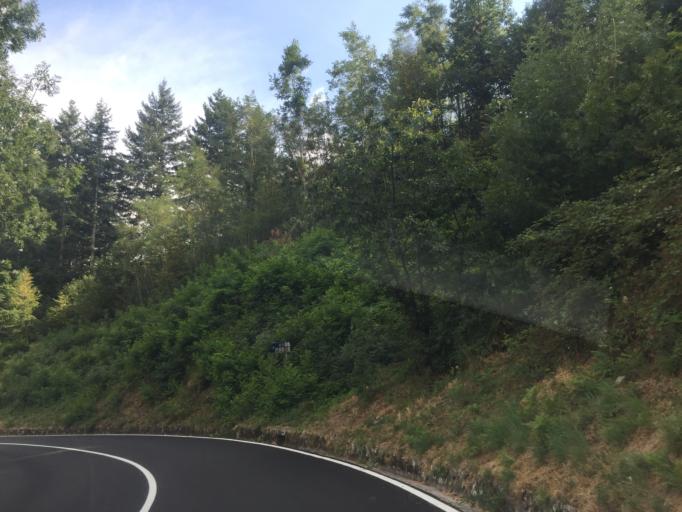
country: IT
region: Tuscany
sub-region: Provincia di Pistoia
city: Cutigliano
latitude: 44.1041
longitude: 10.7425
